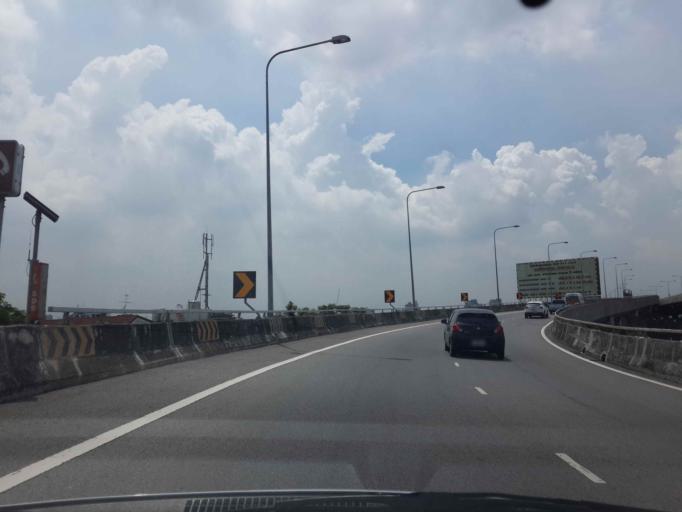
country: TH
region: Bangkok
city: Phra Khanong
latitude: 13.6980
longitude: 100.5926
